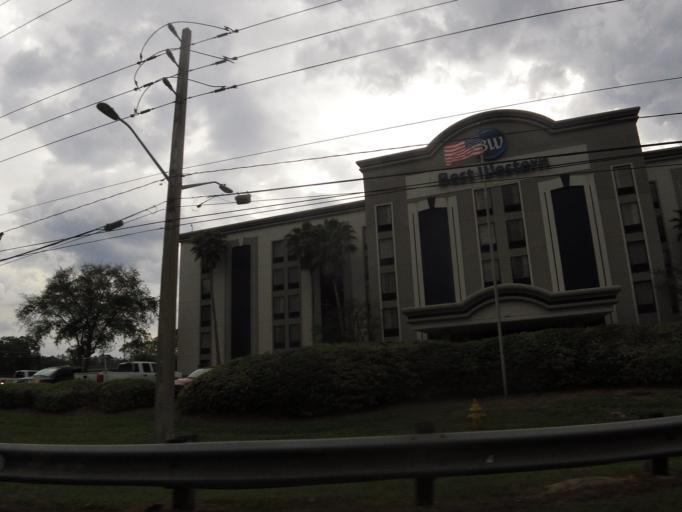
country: US
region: Florida
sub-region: Clay County
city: Orange Park
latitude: 30.1932
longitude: -81.7075
